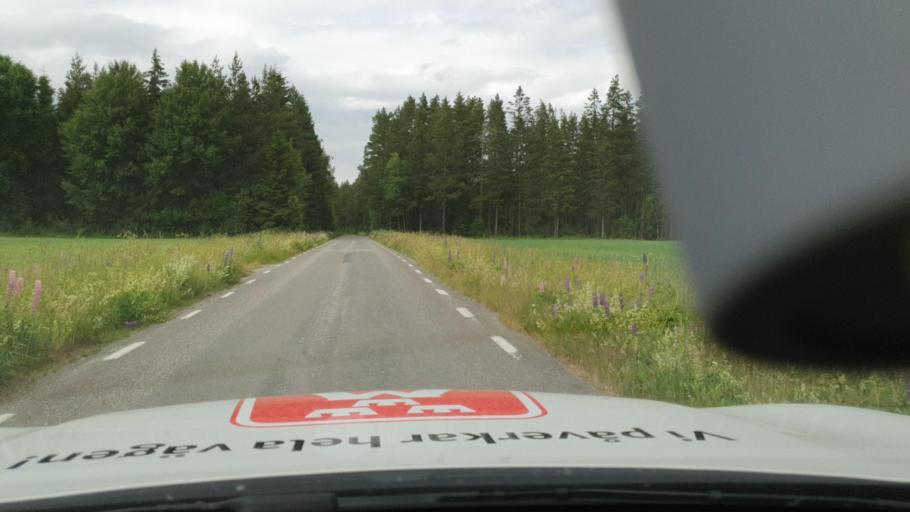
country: SE
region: Vaestra Goetaland
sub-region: Tidaholms Kommun
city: Tidaholm
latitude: 58.1719
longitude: 14.0139
